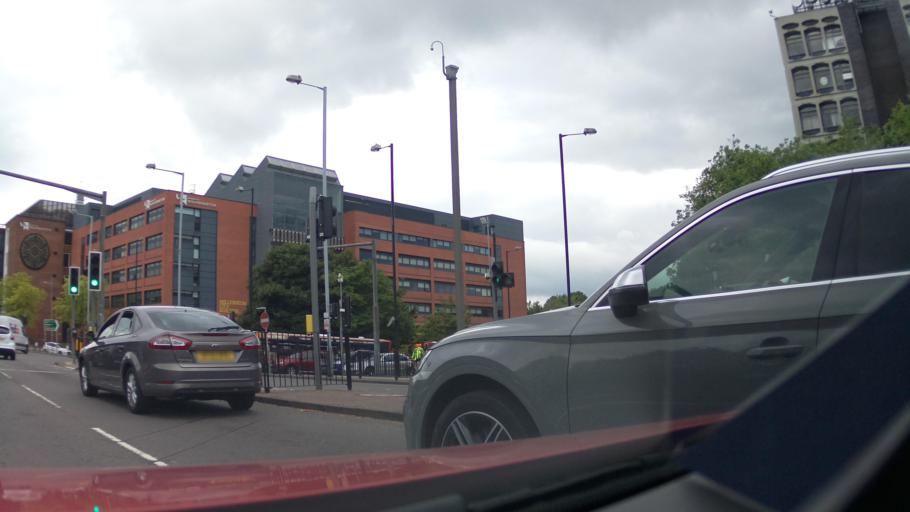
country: GB
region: England
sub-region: Wolverhampton
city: Wolverhampton
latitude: 52.5897
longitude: -2.1266
